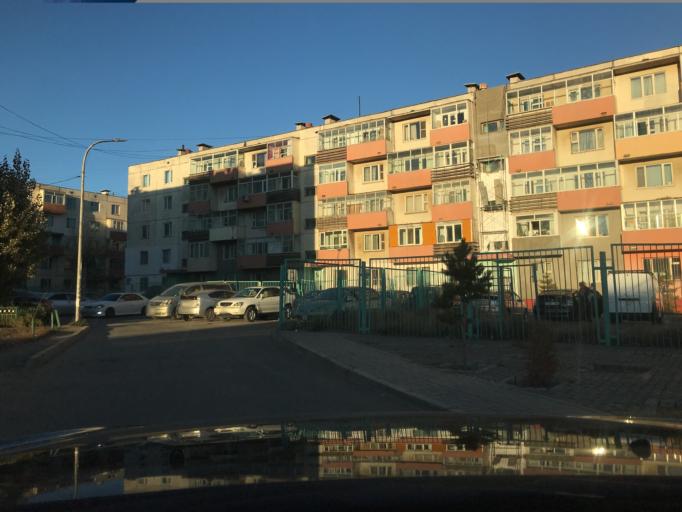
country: MN
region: Ulaanbaatar
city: Ulaanbaatar
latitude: 47.9256
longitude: 106.9087
